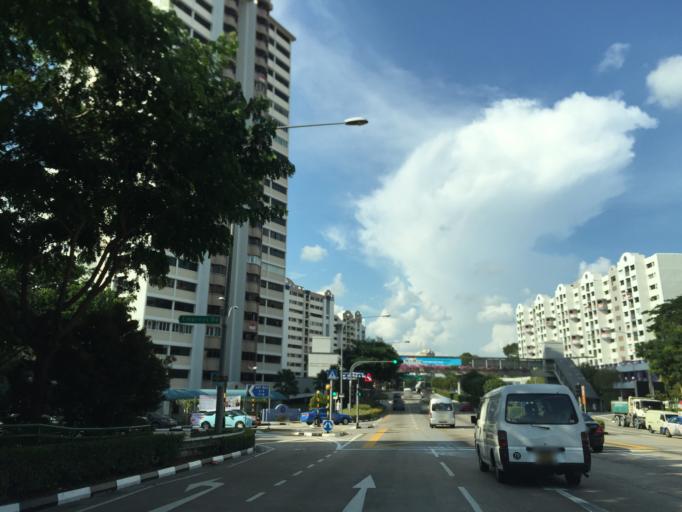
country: SG
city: Singapore
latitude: 1.3165
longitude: 103.8064
